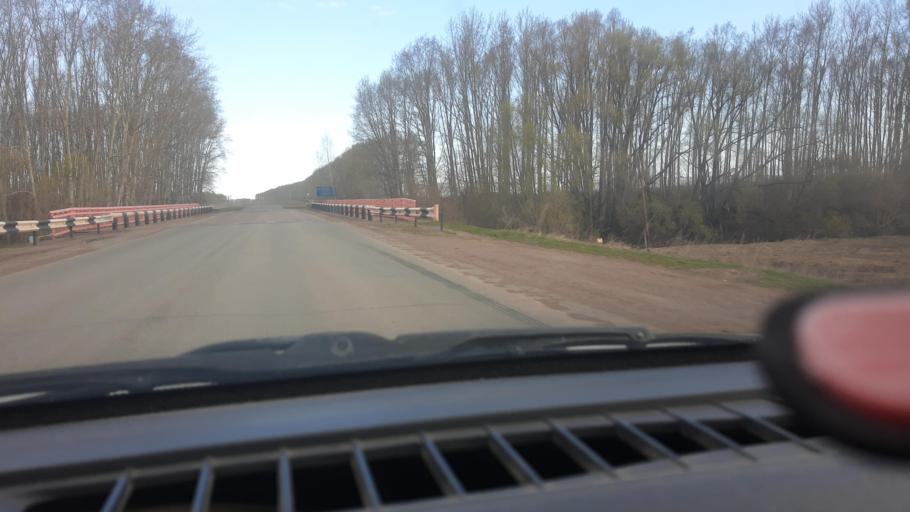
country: RU
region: Bashkortostan
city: Asanovo
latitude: 54.9701
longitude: 55.5394
